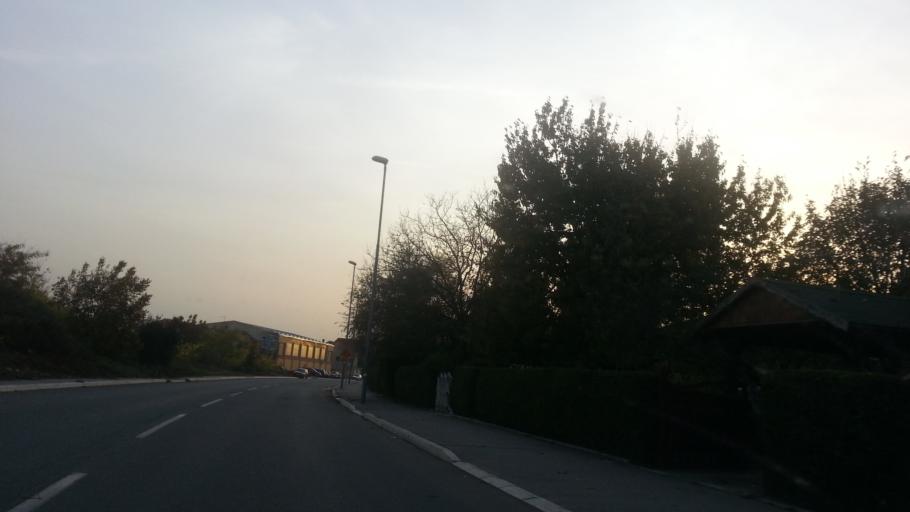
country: RS
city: Novi Banovci
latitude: 44.8927
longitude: 20.2945
